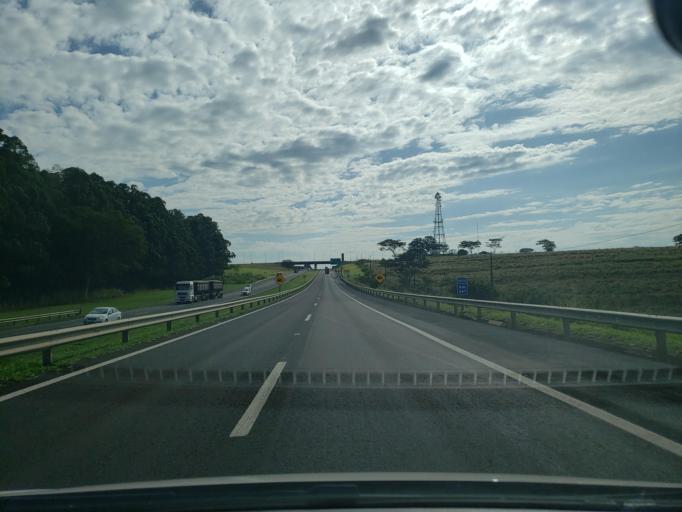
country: BR
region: Sao Paulo
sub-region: Lins
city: Lins
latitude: -21.6689
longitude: -49.7848
